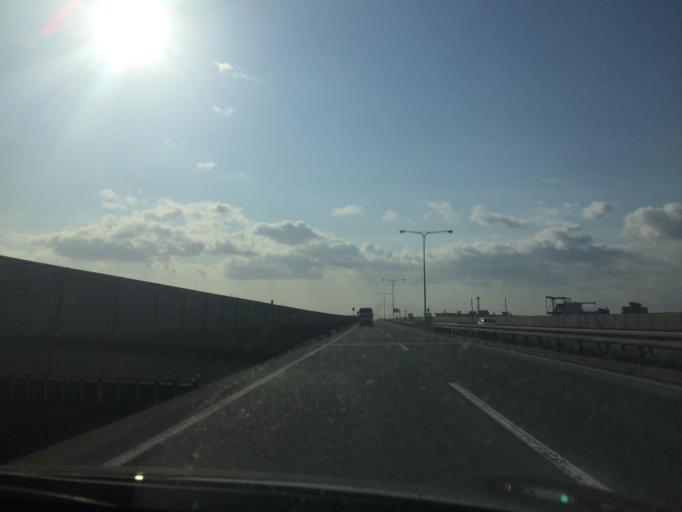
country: JP
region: Hokkaido
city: Sapporo
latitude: 43.0540
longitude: 141.4290
